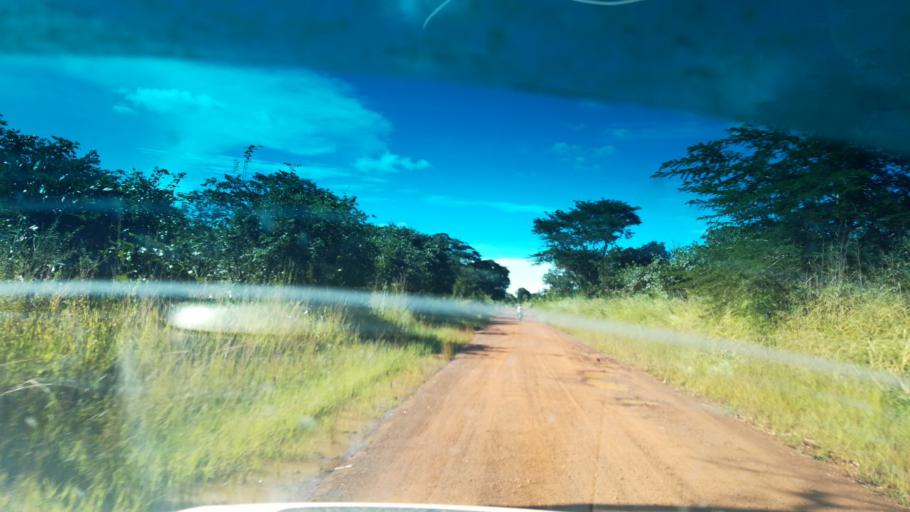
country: ZM
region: Luapula
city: Nchelenge
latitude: -9.3961
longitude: 28.1988
